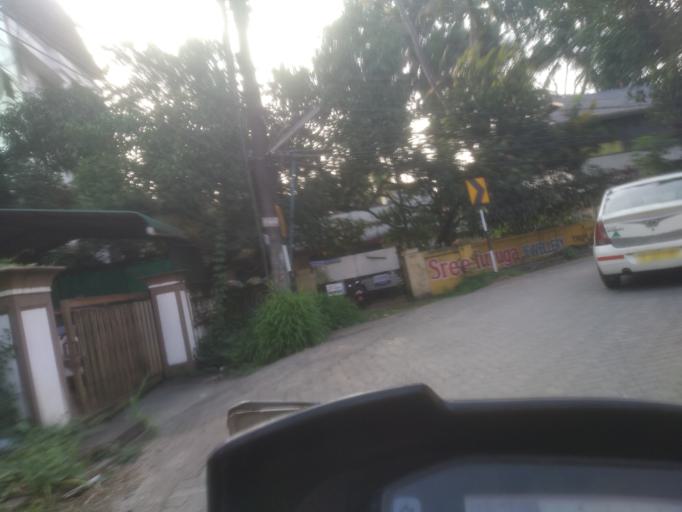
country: IN
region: Kerala
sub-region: Alappuzha
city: Arukutti
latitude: 9.9382
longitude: 76.3493
